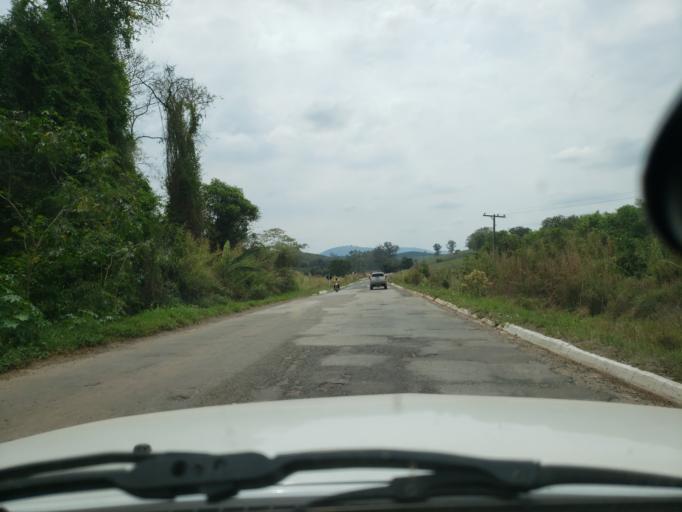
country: BR
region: Minas Gerais
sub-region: Jacutinga
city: Jacutinga
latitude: -22.2685
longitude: -46.6051
